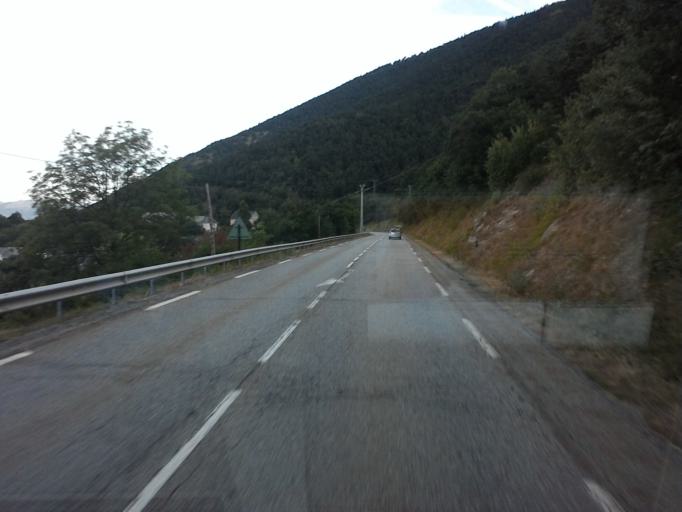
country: FR
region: Rhone-Alpes
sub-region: Departement de l'Isere
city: La Mure
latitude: 44.8379
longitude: 5.8780
